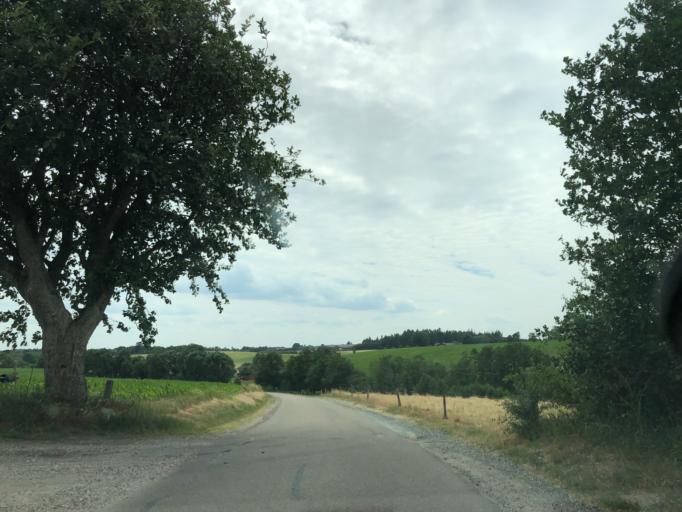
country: DK
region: Central Jutland
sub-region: Silkeborg Kommune
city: Svejbaek
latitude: 56.2024
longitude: 9.6901
